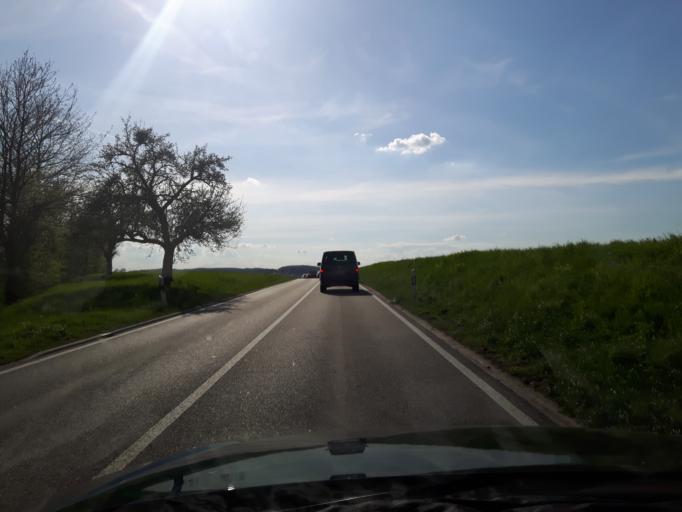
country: DE
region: Baden-Wuerttemberg
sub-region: Regierungsbezirk Stuttgart
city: Bretzfeld
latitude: 49.1887
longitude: 9.4279
